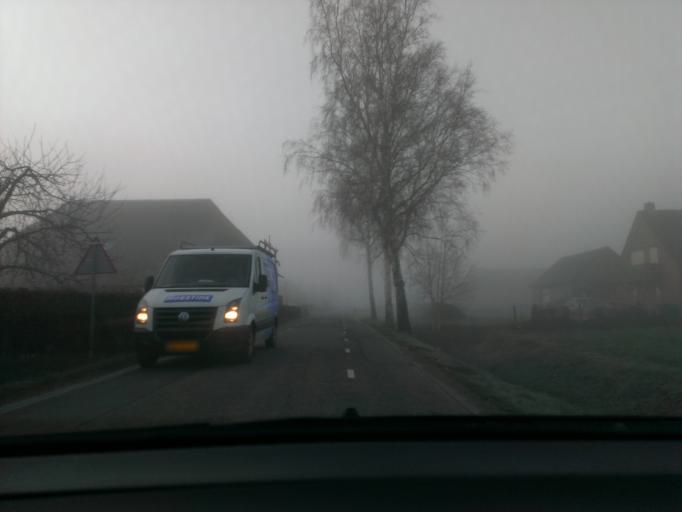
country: NL
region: Gelderland
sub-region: Gemeente Voorst
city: Twello
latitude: 52.2630
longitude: 6.0589
